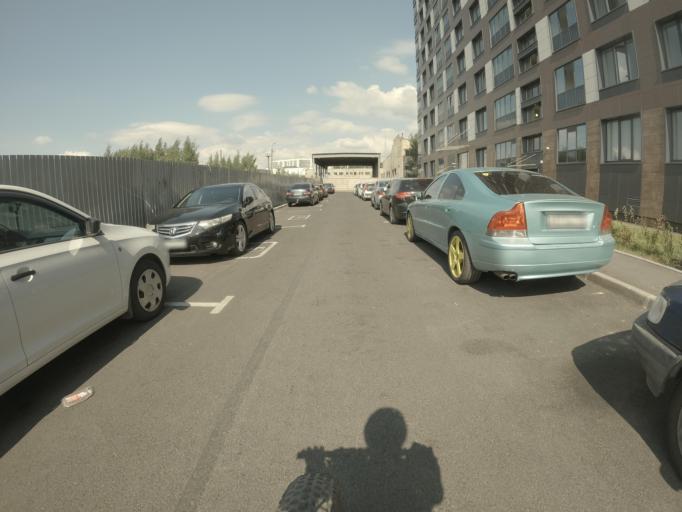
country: RU
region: St.-Petersburg
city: Obukhovo
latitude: 59.9073
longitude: 30.4415
